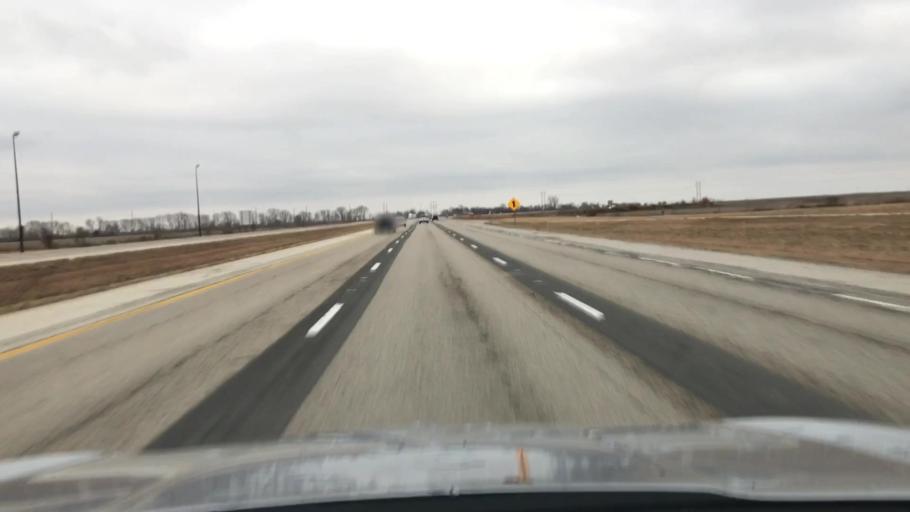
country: US
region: Illinois
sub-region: Logan County
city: Lincoln
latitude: 40.1091
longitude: -89.4166
